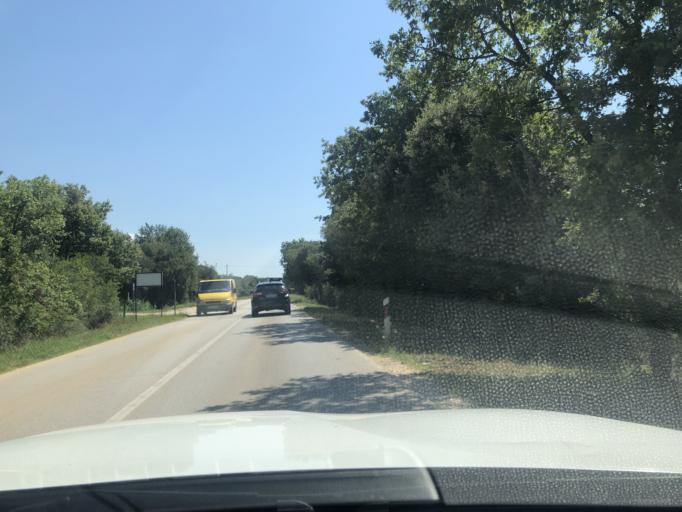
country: HR
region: Istarska
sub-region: Grad Rovinj
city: Rovinj
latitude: 45.0482
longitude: 13.7421
